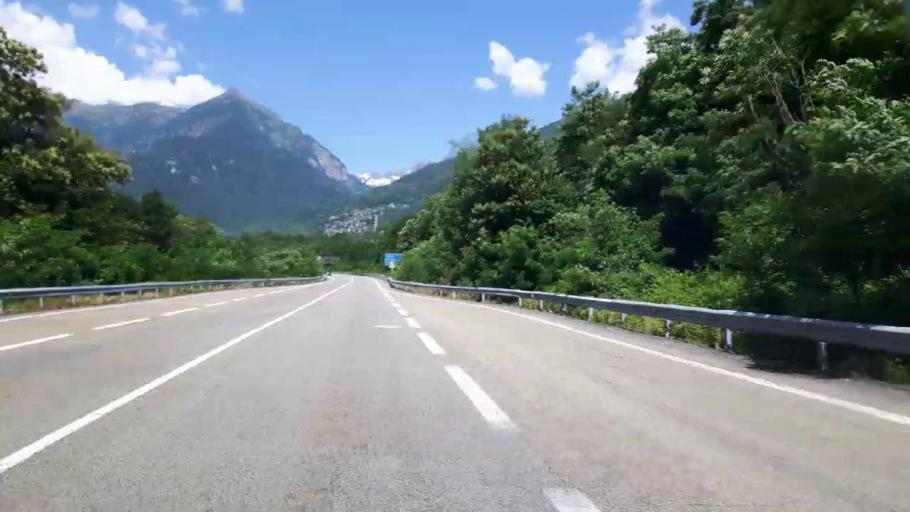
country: IT
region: Piedmont
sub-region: Provincia Verbano-Cusio-Ossola
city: Varzo
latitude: 46.1979
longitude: 8.2701
